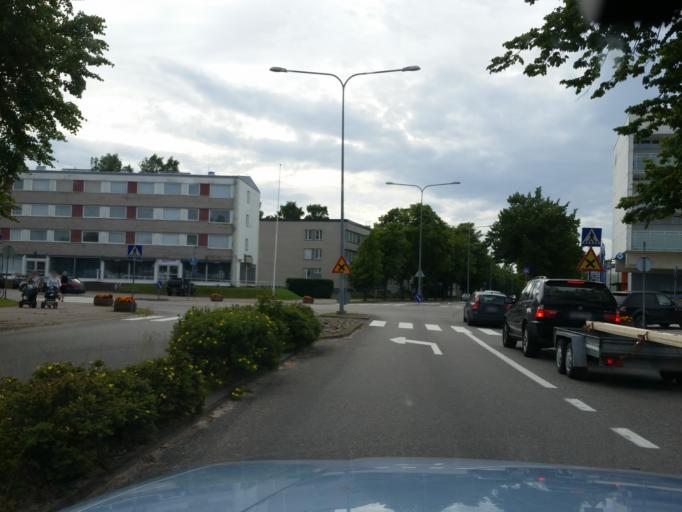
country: FI
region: Uusimaa
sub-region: Raaseporin
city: Hanko
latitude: 59.8284
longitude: 22.9667
